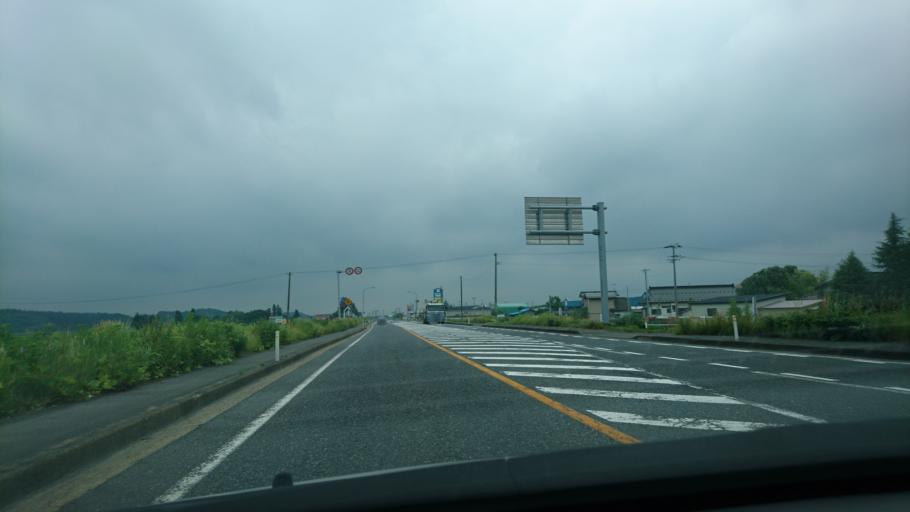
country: JP
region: Miyagi
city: Furukawa
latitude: 38.6702
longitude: 140.8663
